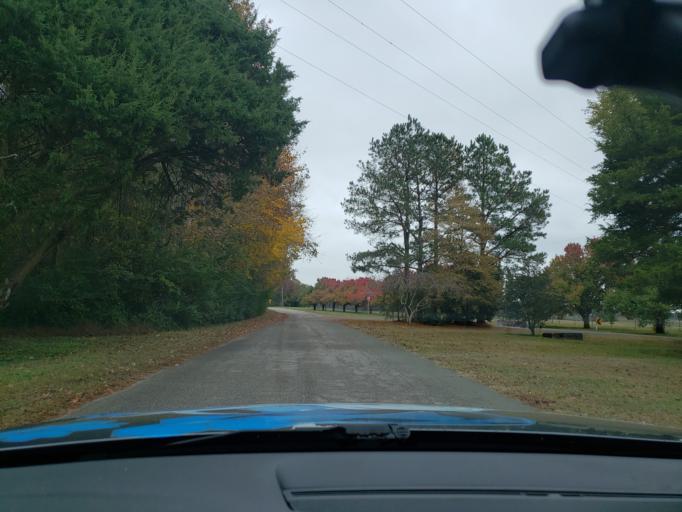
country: US
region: Virginia
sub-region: City of Chesapeake
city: Chesapeake
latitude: 36.7084
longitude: -76.1275
